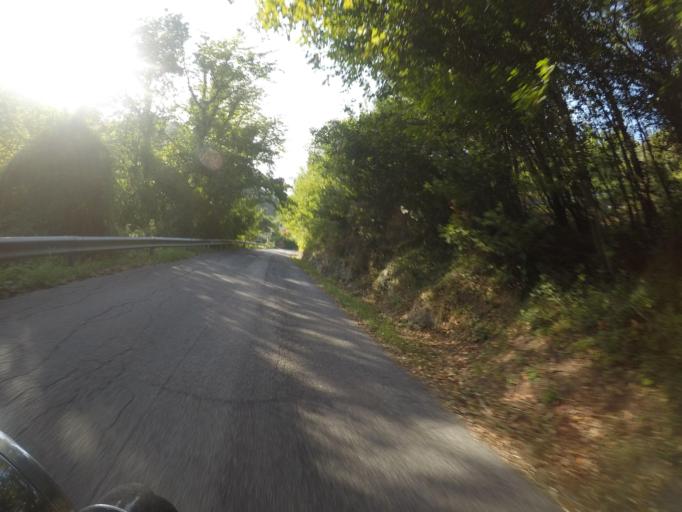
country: IT
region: Tuscany
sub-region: Provincia di Massa-Carrara
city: Carrara
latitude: 44.0845
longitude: 10.0904
